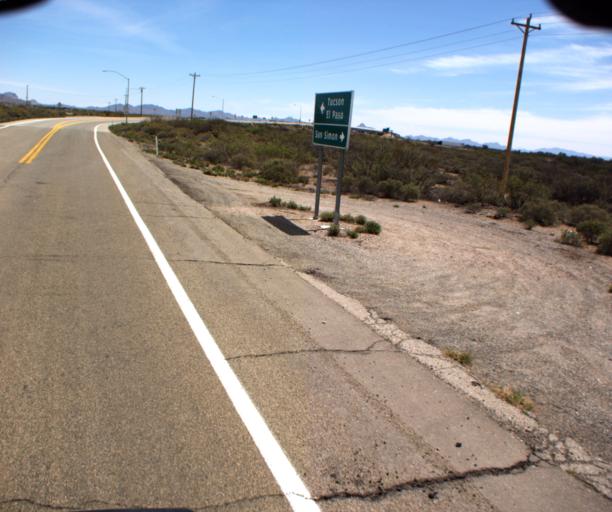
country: US
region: New Mexico
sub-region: Hidalgo County
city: Lordsburg
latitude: 32.2600
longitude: -109.1987
